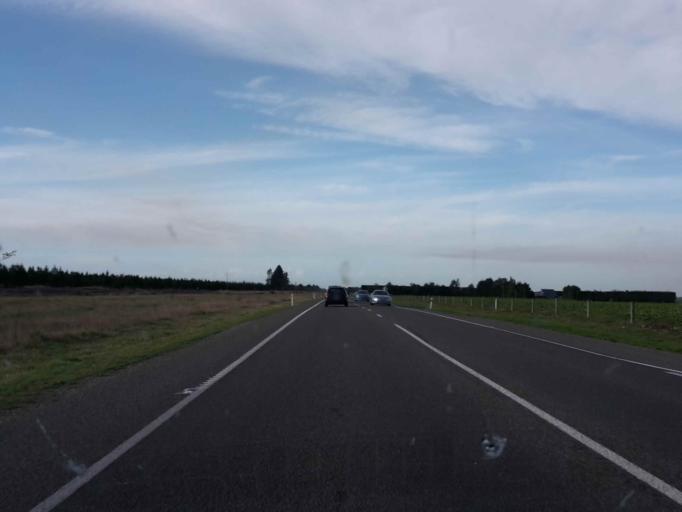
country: NZ
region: Canterbury
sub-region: Ashburton District
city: Tinwald
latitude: -43.9672
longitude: 171.6333
